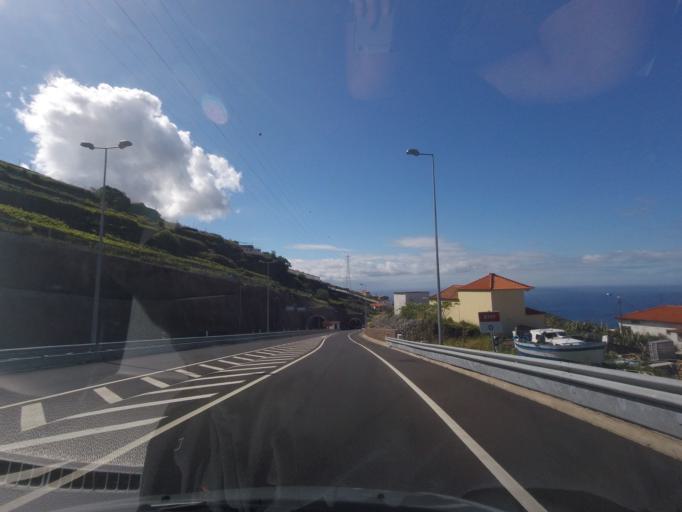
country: PT
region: Madeira
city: Camara de Lobos
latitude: 32.6680
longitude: -16.9705
